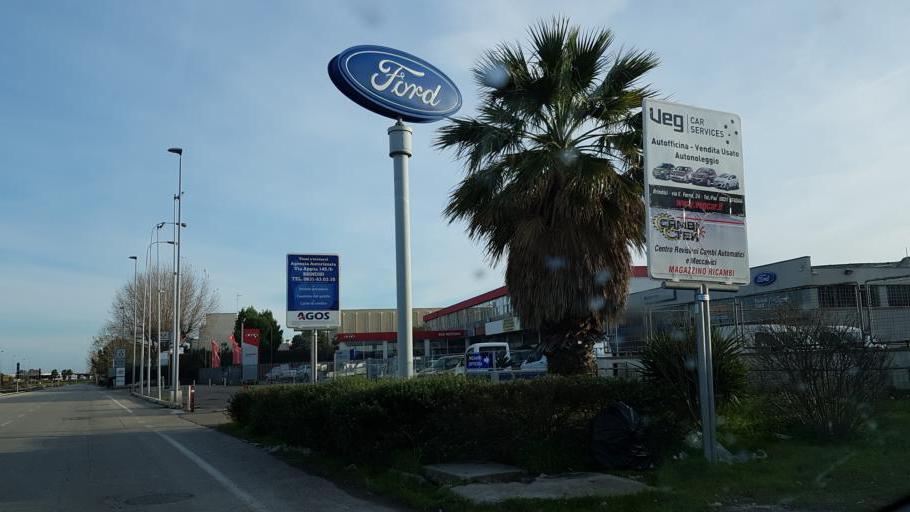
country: IT
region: Apulia
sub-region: Provincia di Brindisi
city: Brindisi
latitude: 40.6312
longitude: 17.9568
